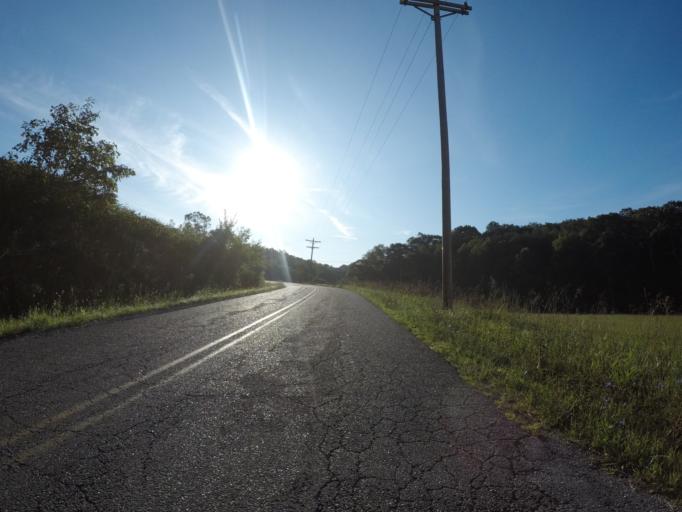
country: US
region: Ohio
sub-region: Lawrence County
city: Coal Grove
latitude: 38.6003
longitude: -82.5669
